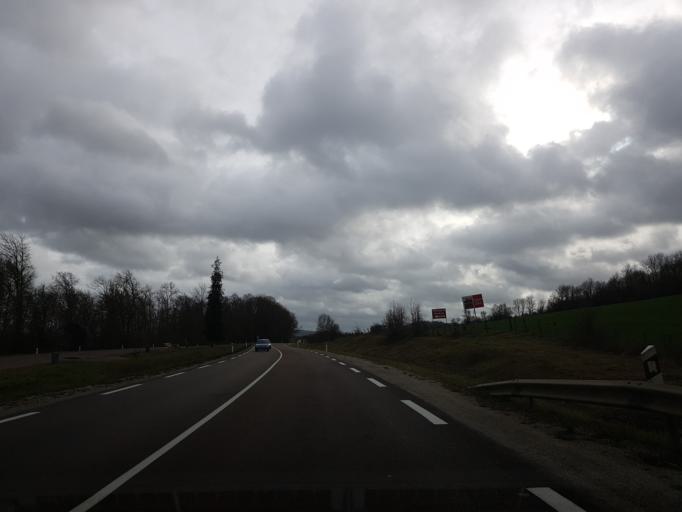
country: FR
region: Champagne-Ardenne
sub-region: Departement de la Haute-Marne
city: Rolampont
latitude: 47.9132
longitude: 5.2899
